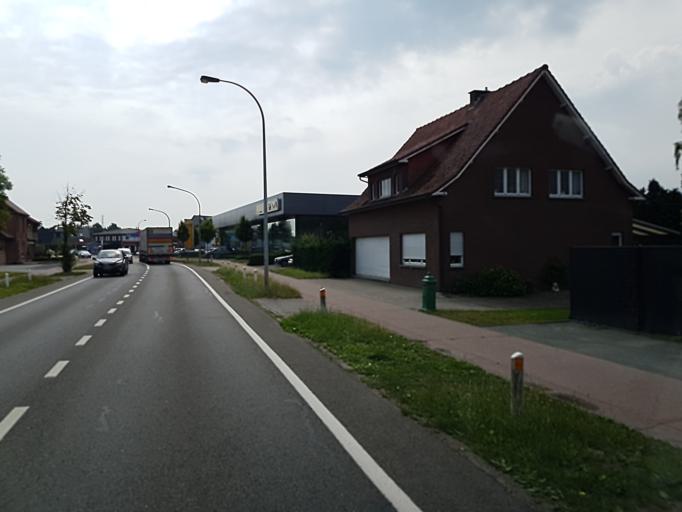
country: BE
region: Flanders
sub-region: Provincie Antwerpen
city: Mol
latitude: 51.1749
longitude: 5.1352
